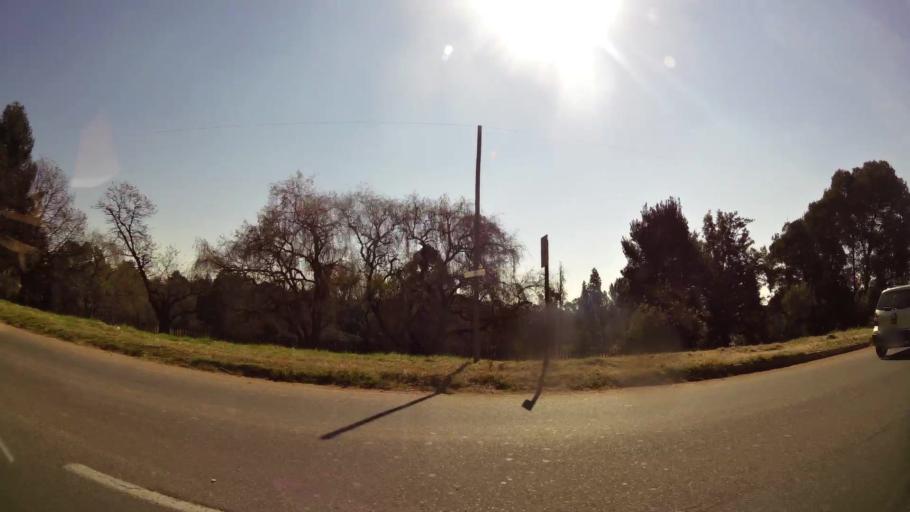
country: ZA
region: Gauteng
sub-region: City of Johannesburg Metropolitan Municipality
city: Johannesburg
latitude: -26.1630
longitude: 28.1103
